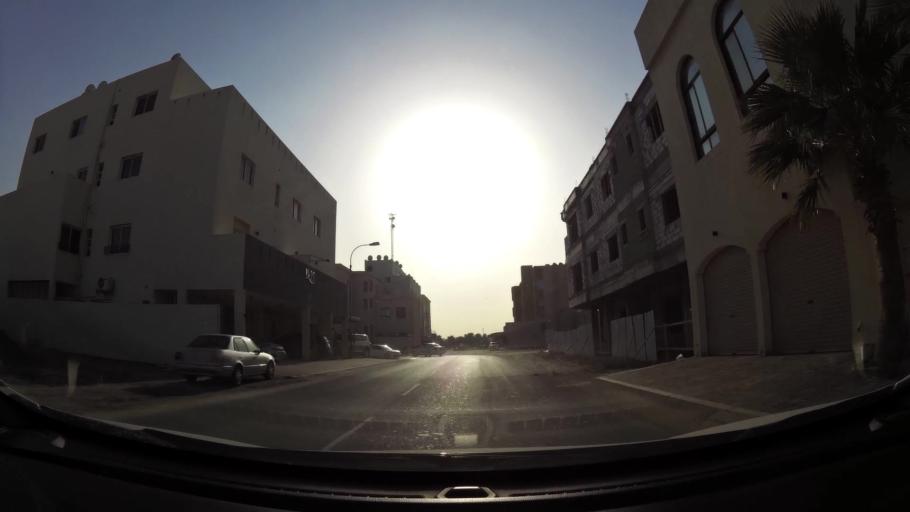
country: BH
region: Manama
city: Jidd Hafs
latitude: 26.2090
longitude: 50.4998
